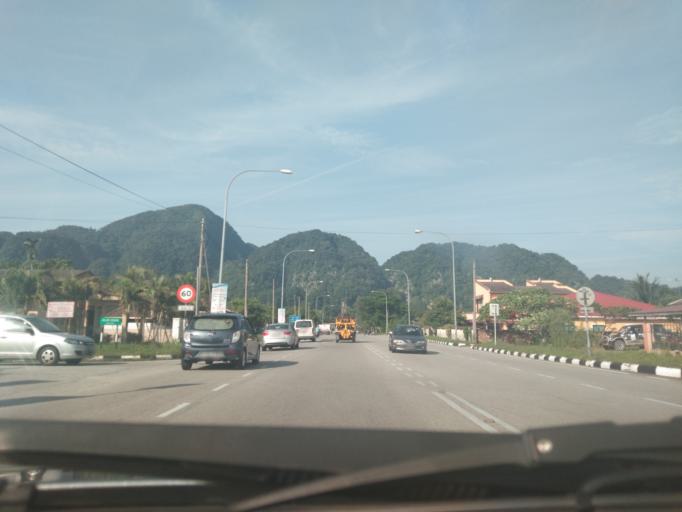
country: MY
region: Perak
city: Ipoh
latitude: 4.5703
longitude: 101.1251
